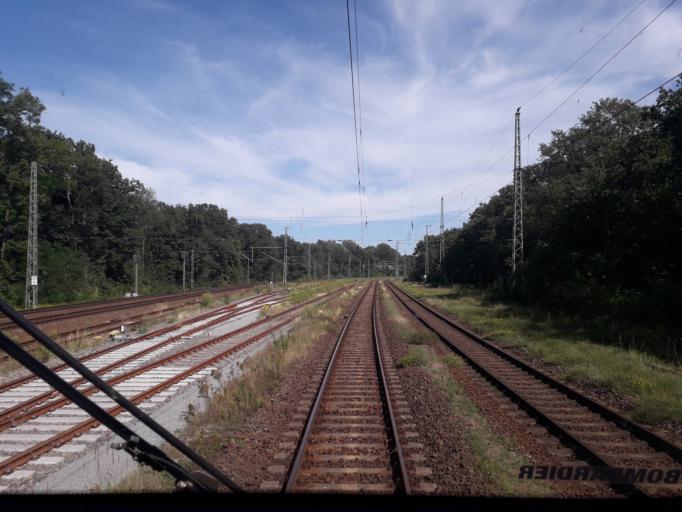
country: DE
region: Brandenburg
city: Potsdam
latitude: 52.3991
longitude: 13.0006
